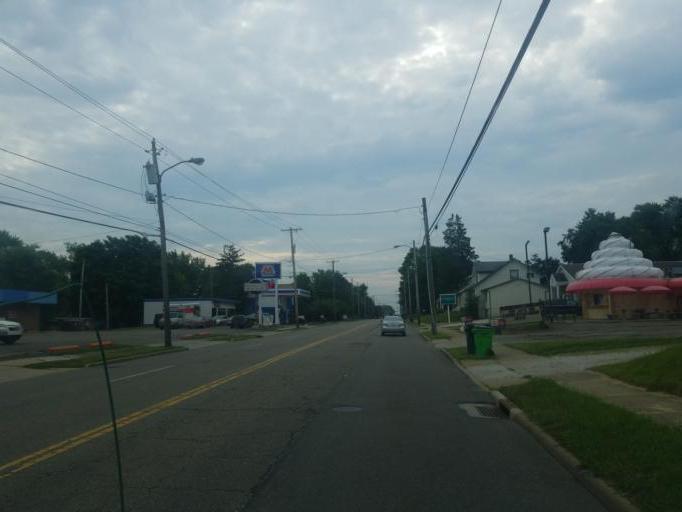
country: US
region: Ohio
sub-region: Stark County
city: Massillon
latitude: 40.7956
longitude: -81.5570
